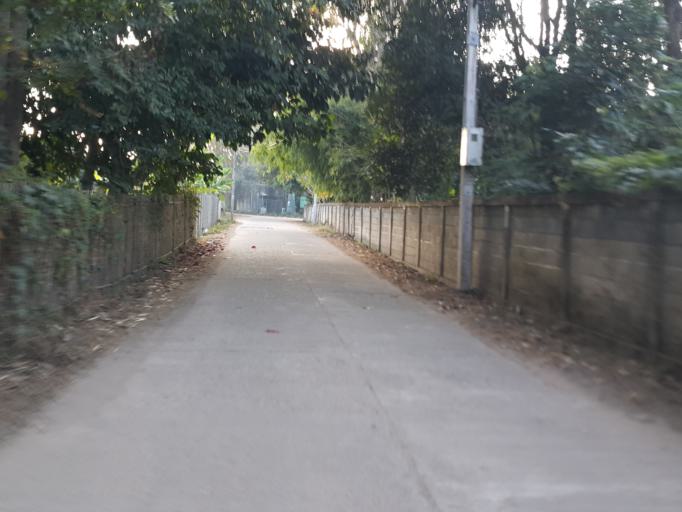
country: TH
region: Chiang Mai
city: Mae On
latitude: 18.7489
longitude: 99.2464
